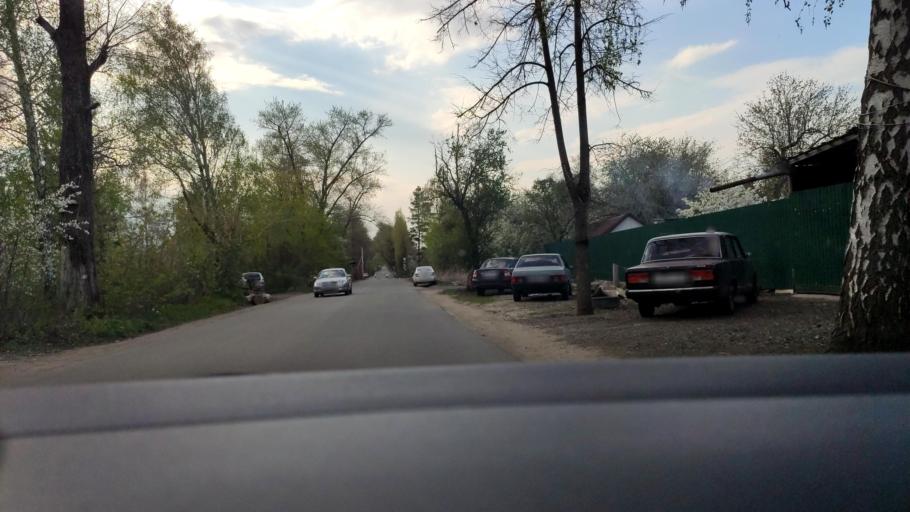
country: RU
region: Voronezj
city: Voronezh
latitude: 51.6006
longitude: 39.1644
